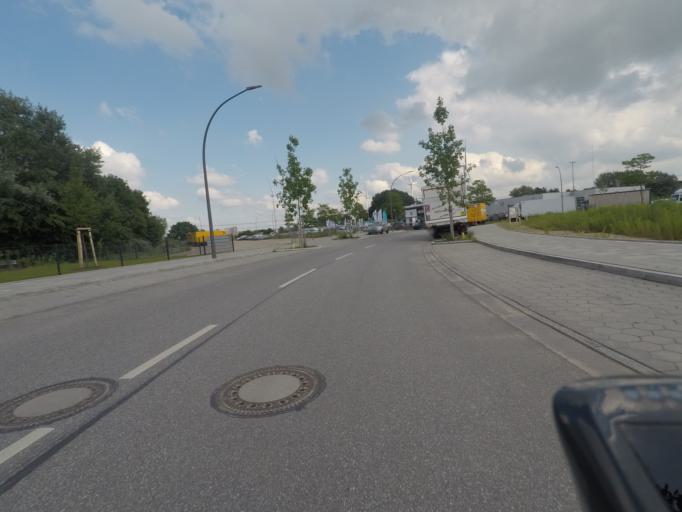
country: DE
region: Hamburg
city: Bergedorf
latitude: 53.4779
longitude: 10.2040
